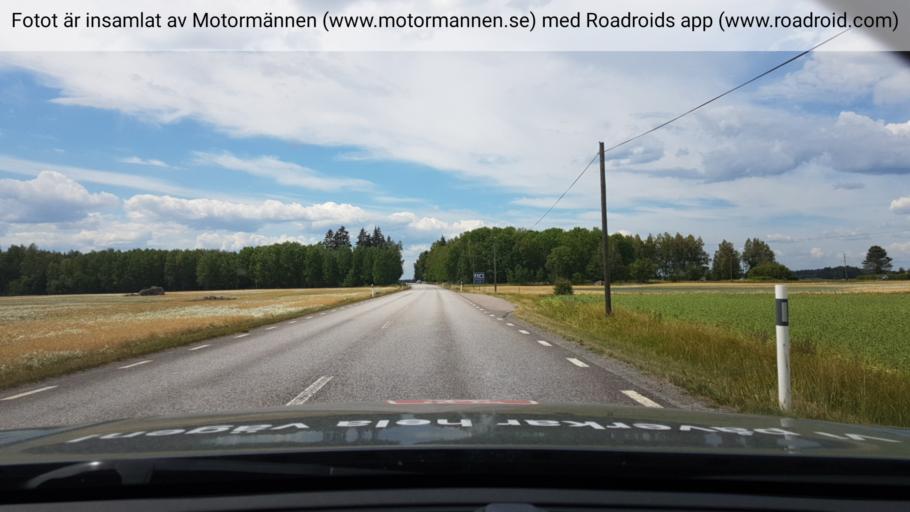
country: SE
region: Vaestmanland
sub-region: Sala Kommun
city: Sala
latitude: 59.8487
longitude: 16.6605
